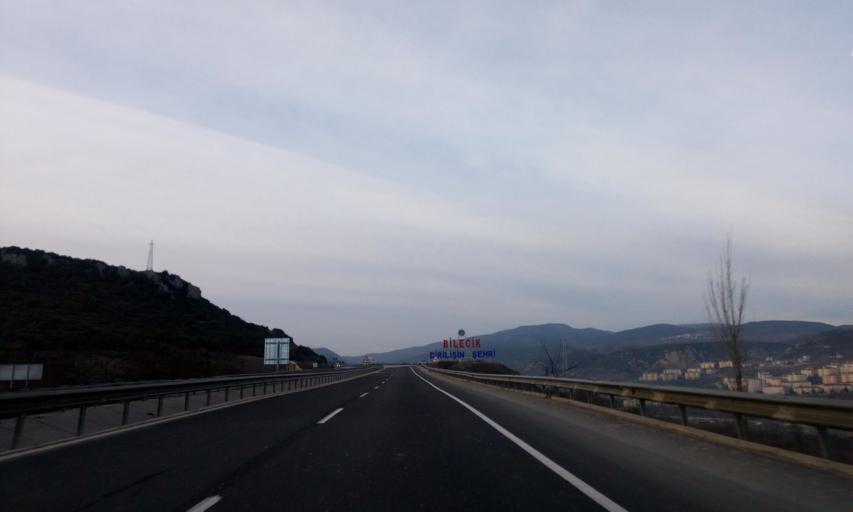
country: TR
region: Bilecik
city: Kuplu
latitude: 40.1314
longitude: 30.0180
